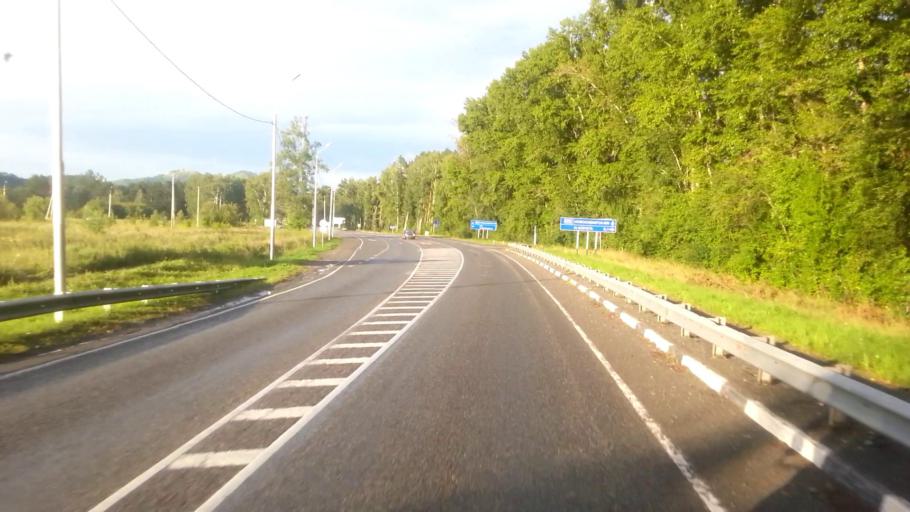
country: RU
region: Altay
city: Souzga
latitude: 51.8803
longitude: 85.8288
